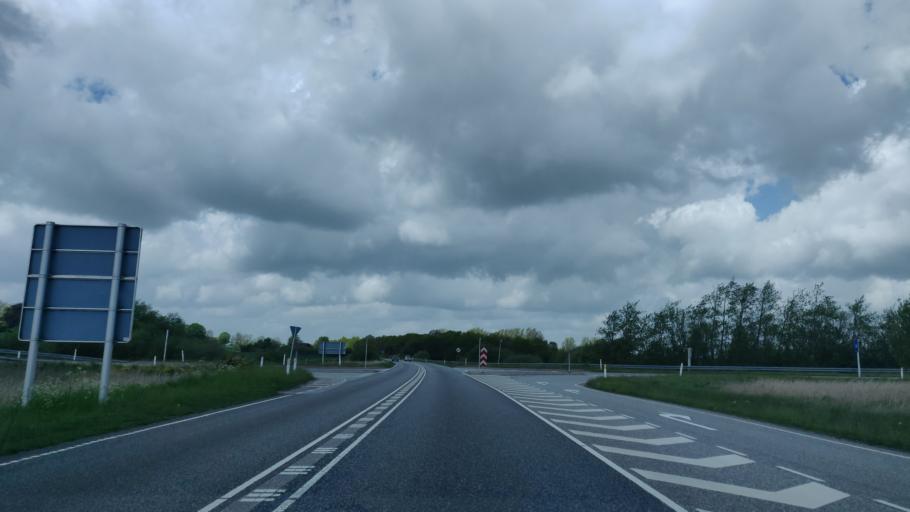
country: DK
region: Central Jutland
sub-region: Hedensted Kommune
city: Torring
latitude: 55.8383
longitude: 9.5085
